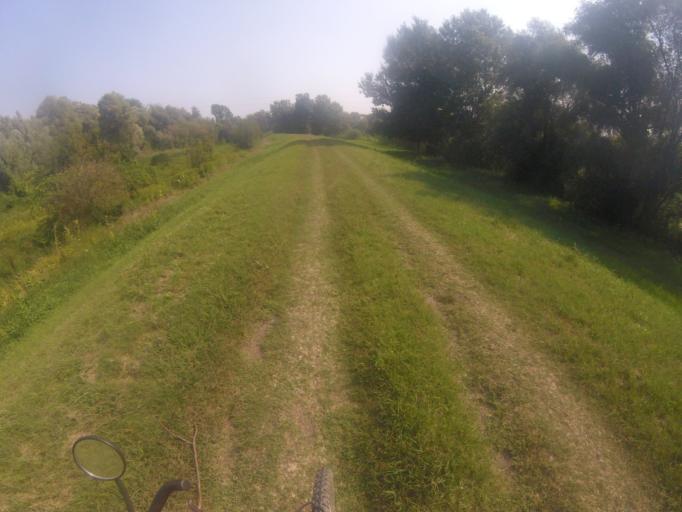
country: HU
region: Bacs-Kiskun
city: Baja
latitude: 46.1956
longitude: 18.9494
